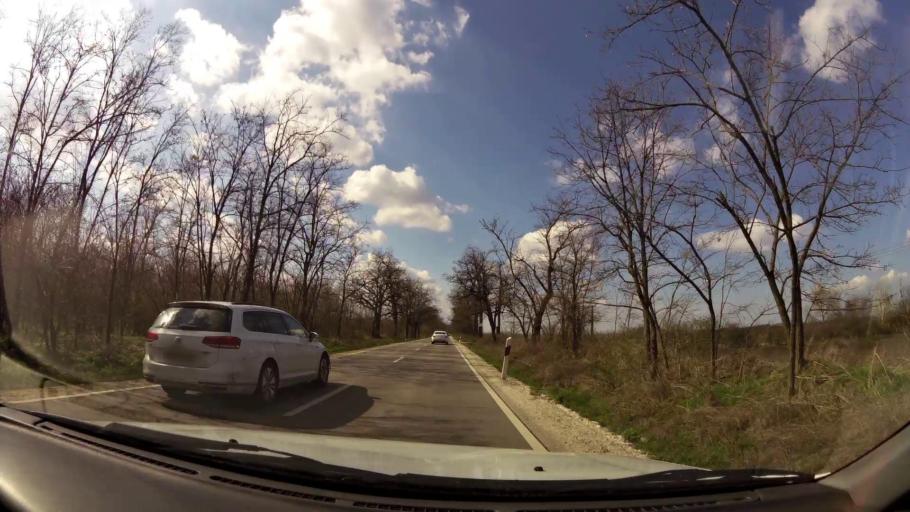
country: HU
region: Pest
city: Forropuszta
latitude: 47.4565
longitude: 19.6680
